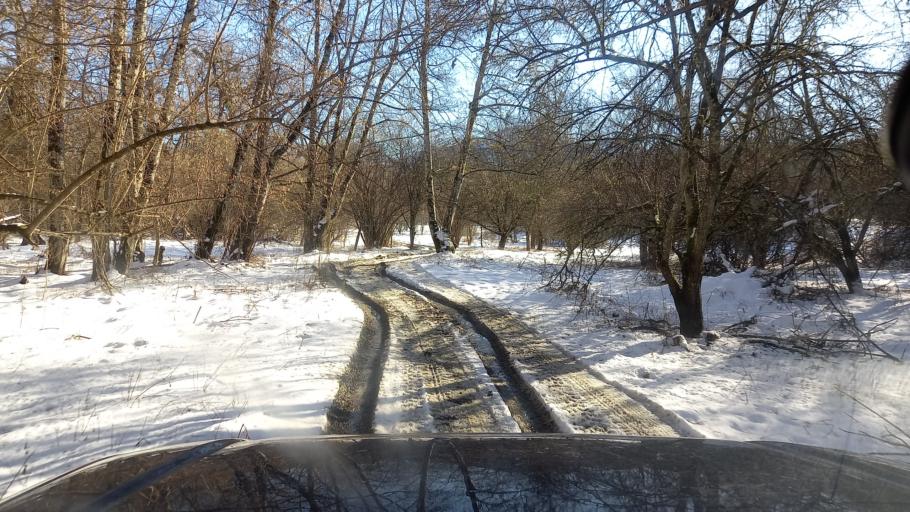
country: RU
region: Adygeya
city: Kamennomostskiy
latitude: 44.2065
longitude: 40.1478
